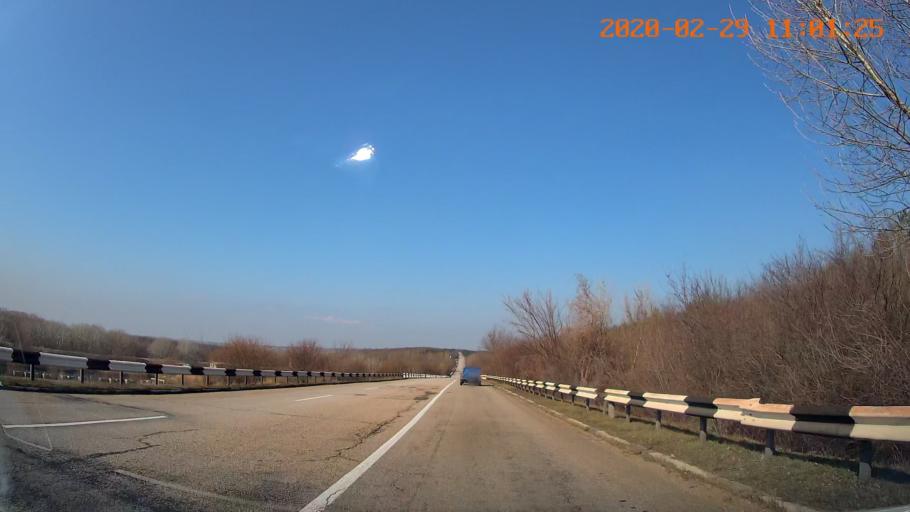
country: MD
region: Telenesti
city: Grigoriopol
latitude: 47.1638
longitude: 29.2589
